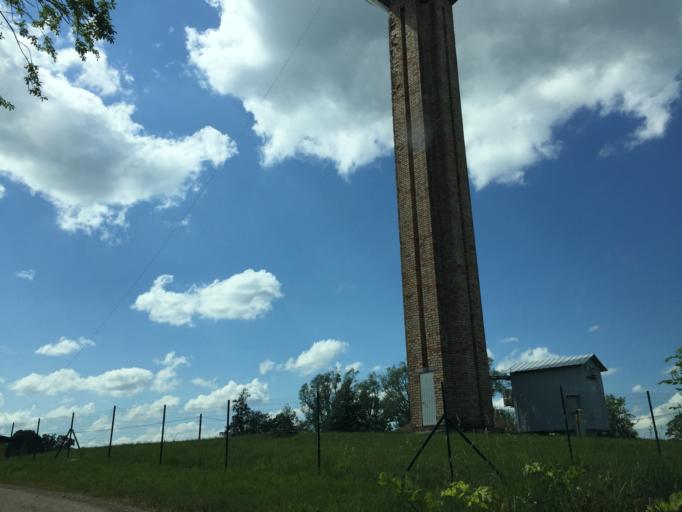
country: LV
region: Priekuli
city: Priekuli
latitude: 57.2604
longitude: 25.4254
